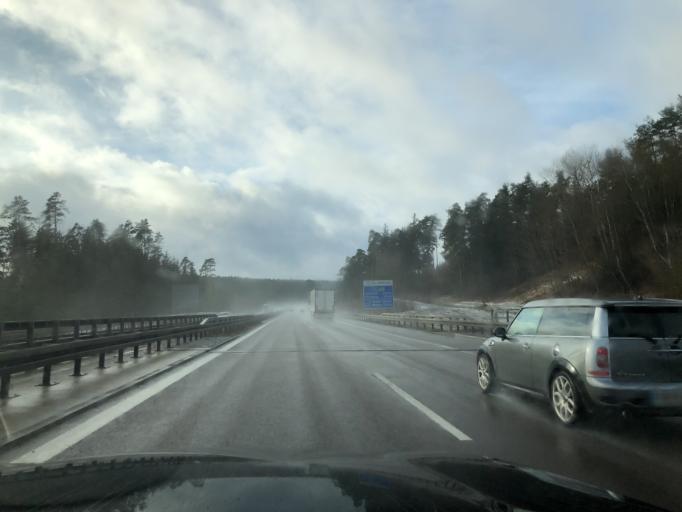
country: DE
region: Bavaria
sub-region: Upper Palatinate
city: Kummersbruck
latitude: 49.3945
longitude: 11.9037
